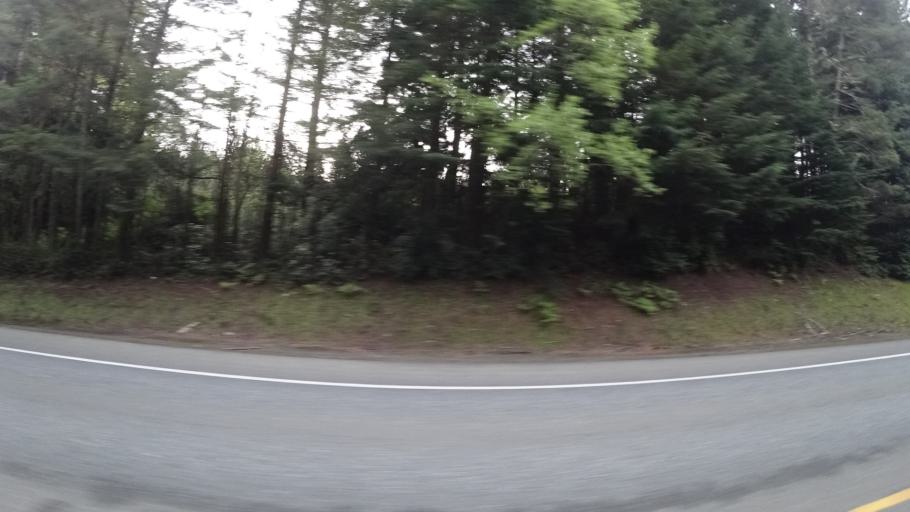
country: US
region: Oregon
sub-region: Coos County
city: Lakeside
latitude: 43.5332
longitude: -124.2156
